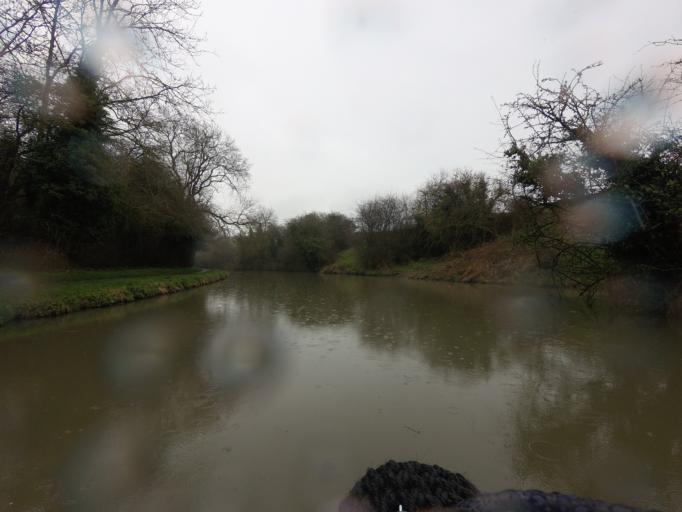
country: GB
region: England
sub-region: Northamptonshire
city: Blisworth
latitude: 52.1712
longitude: -0.9409
